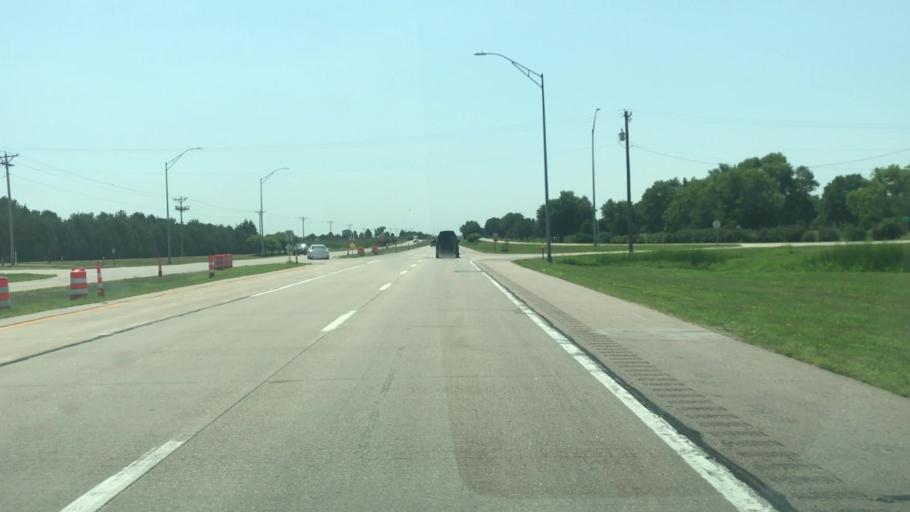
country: US
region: Nebraska
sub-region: Adams County
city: Hastings
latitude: 40.6413
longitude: -98.3820
